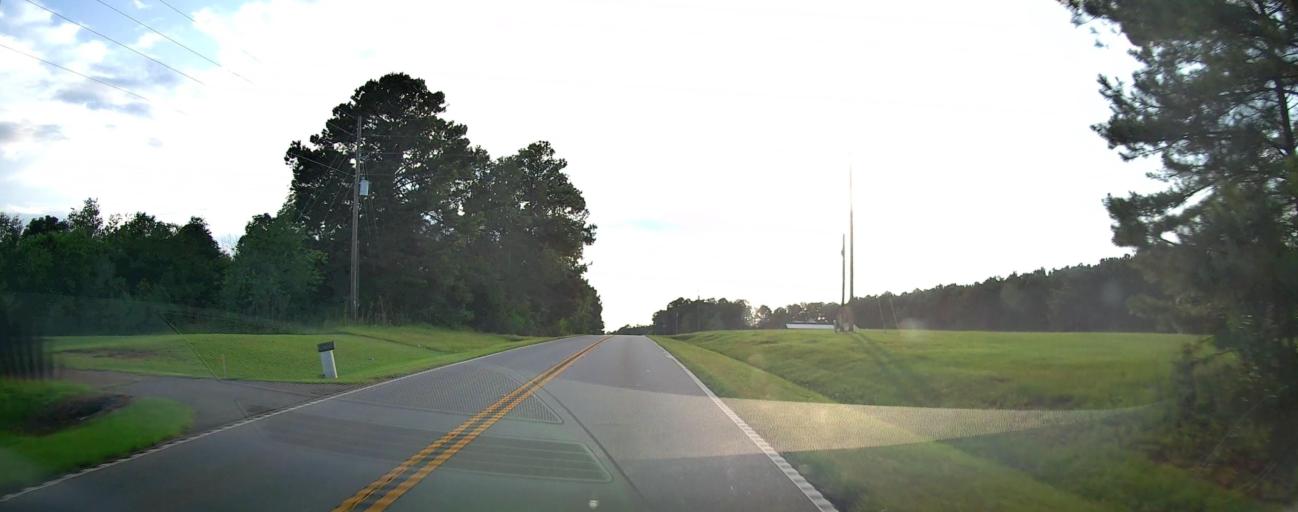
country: US
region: Georgia
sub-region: Peach County
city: Fort Valley
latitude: 32.5583
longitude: -83.9174
